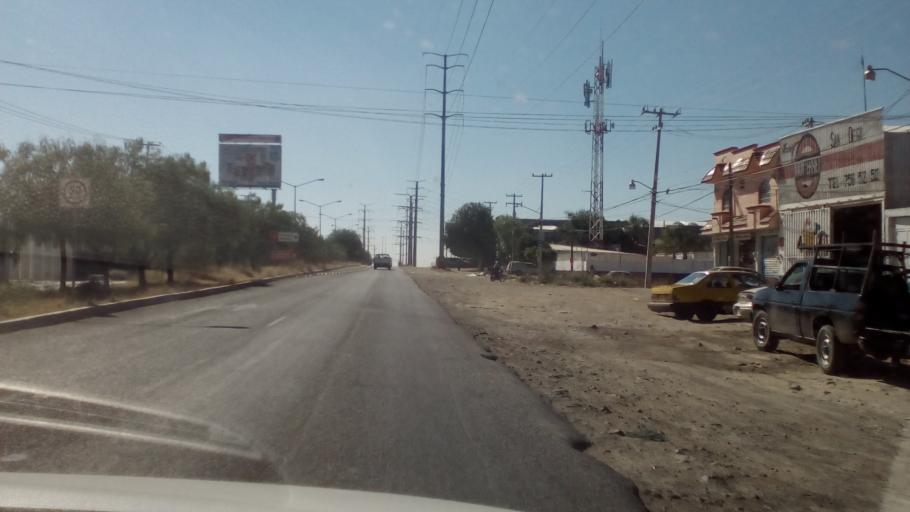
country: MX
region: Guanajuato
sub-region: Leon
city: La Ermita
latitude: 21.1464
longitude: -101.7275
